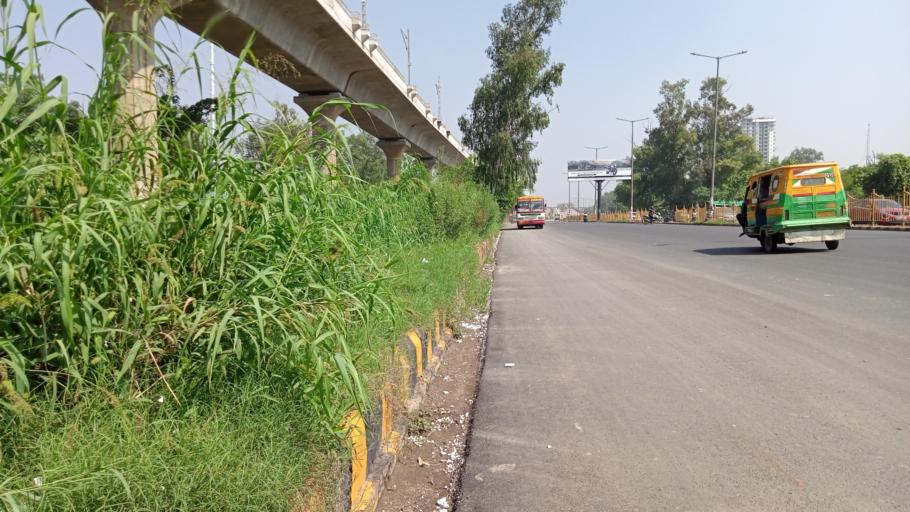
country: IN
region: Uttar Pradesh
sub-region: Ghaziabad
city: Ghaziabad
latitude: 28.6658
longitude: 77.3650
